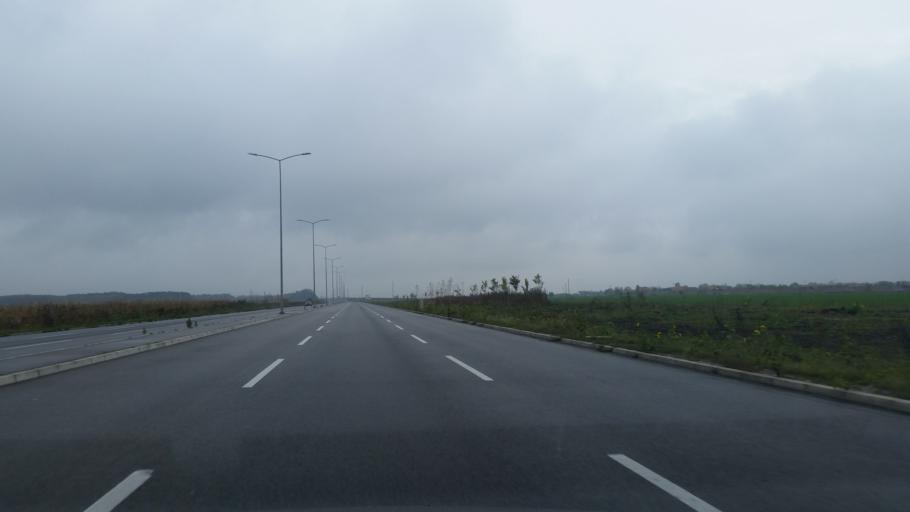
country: RS
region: Central Serbia
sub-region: Belgrade
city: Zemun
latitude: 44.9010
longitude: 20.4357
